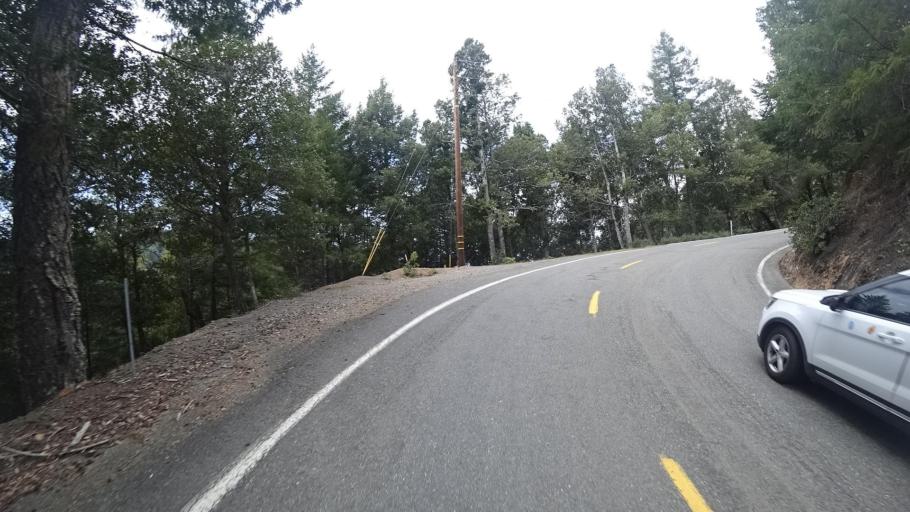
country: US
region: California
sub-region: Humboldt County
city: Redway
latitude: 40.0419
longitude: -124.0232
